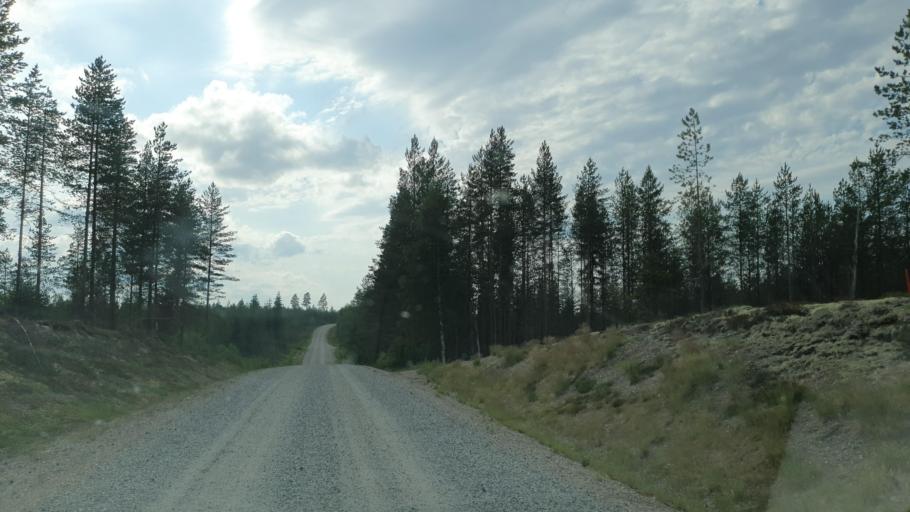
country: FI
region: Kainuu
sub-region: Kehys-Kainuu
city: Kuhmo
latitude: 64.0221
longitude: 29.8881
